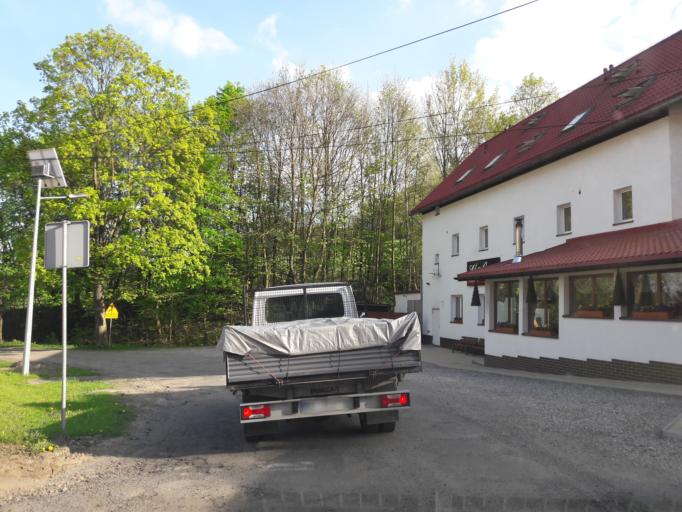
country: PL
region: Lower Silesian Voivodeship
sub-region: Powiat klodzki
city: Duszniki-Zdroj
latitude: 50.4409
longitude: 16.3490
